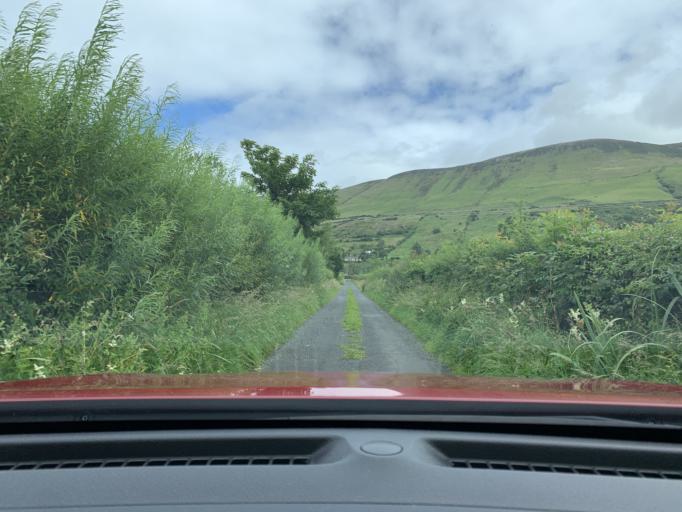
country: IE
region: Connaught
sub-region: Sligo
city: Sligo
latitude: 54.3381
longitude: -8.4814
